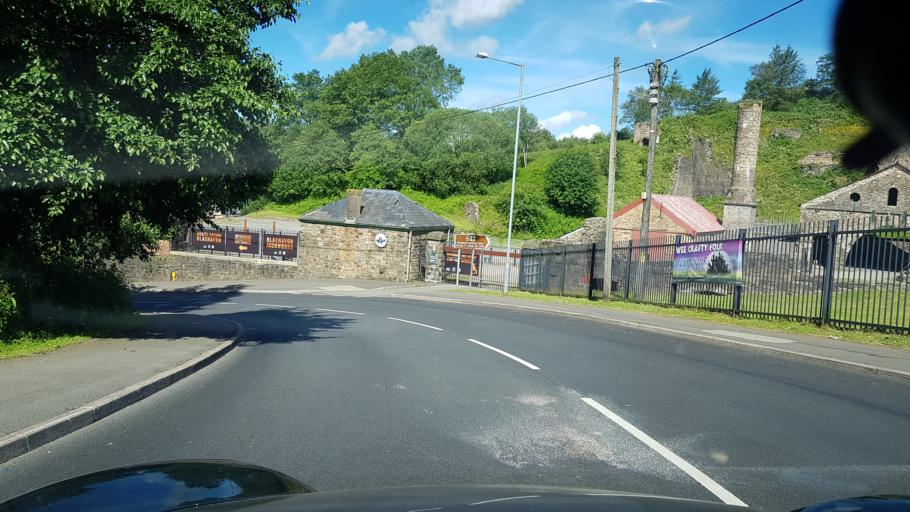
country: GB
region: Wales
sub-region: Torfaen County Borough
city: Blaenavon
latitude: 51.7764
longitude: -3.0886
